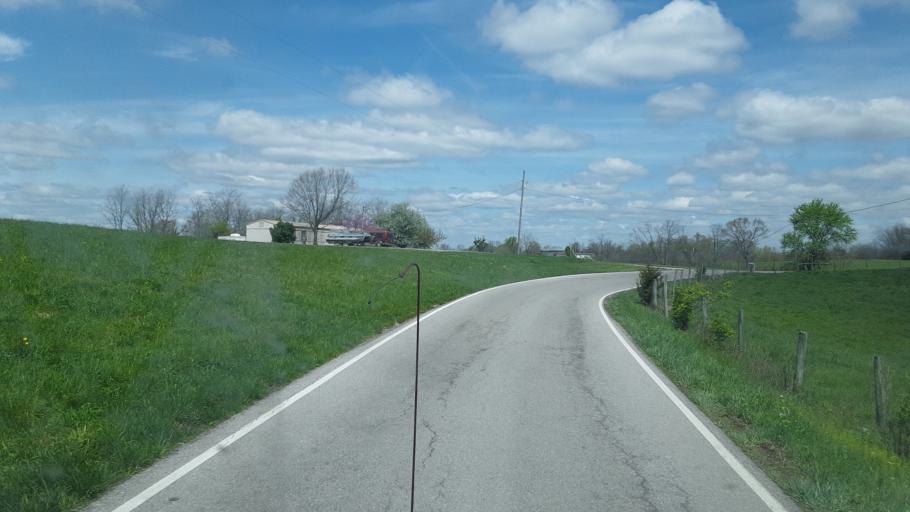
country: US
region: Kentucky
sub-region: Owen County
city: Owenton
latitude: 38.6525
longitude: -84.7723
